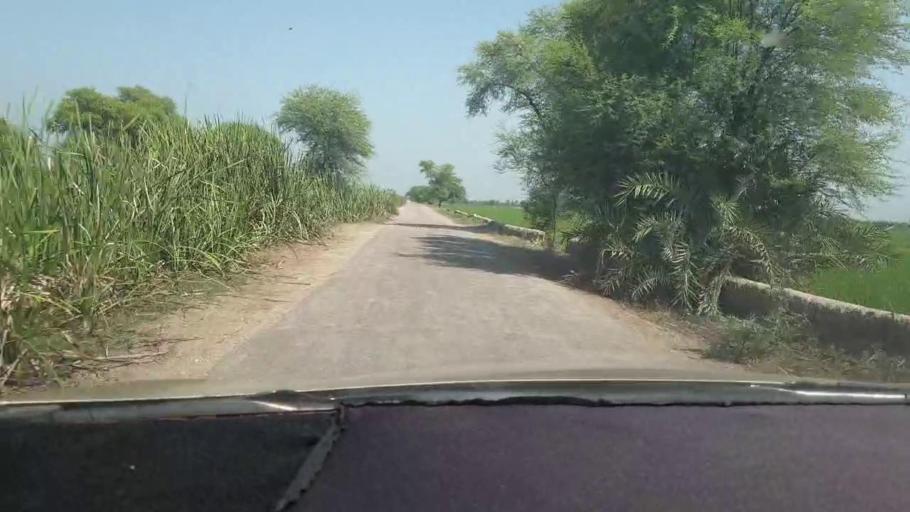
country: PK
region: Sindh
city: Miro Khan
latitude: 27.7067
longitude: 68.0699
